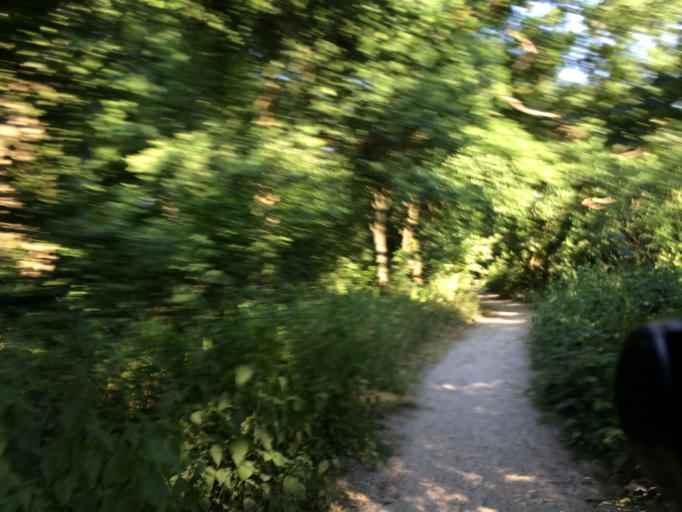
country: FR
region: Ile-de-France
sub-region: Departement de l'Essonne
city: Soisy-sur-Seine
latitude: 48.6521
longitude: 2.4686
